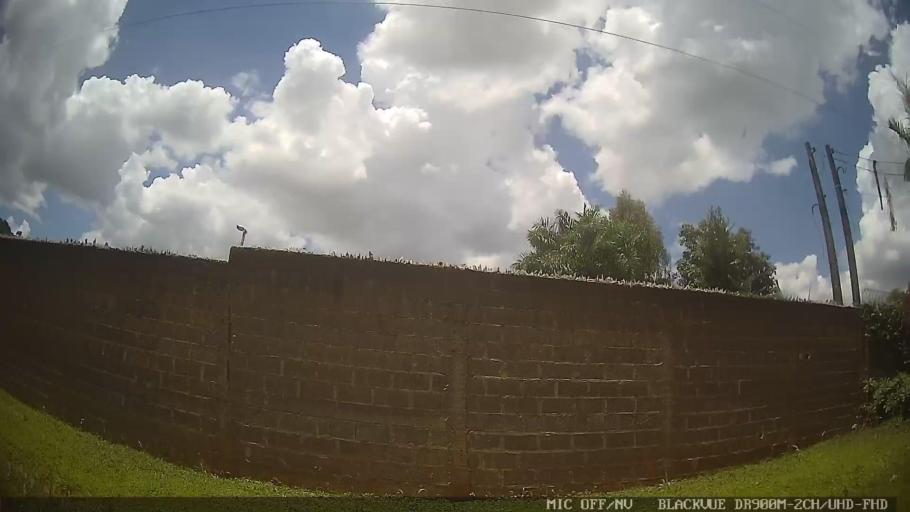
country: BR
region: Sao Paulo
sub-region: Atibaia
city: Atibaia
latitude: -23.1189
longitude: -46.6007
